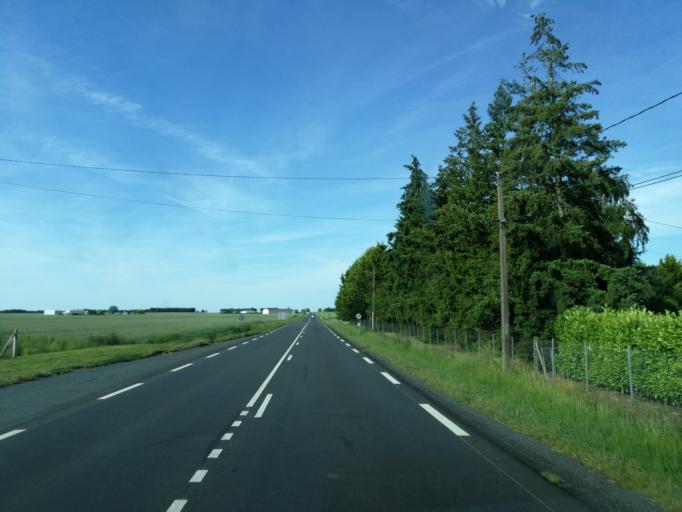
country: FR
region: Centre
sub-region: Departement d'Indre-et-Loire
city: Chateau-Renault
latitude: 47.6118
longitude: 0.9249
